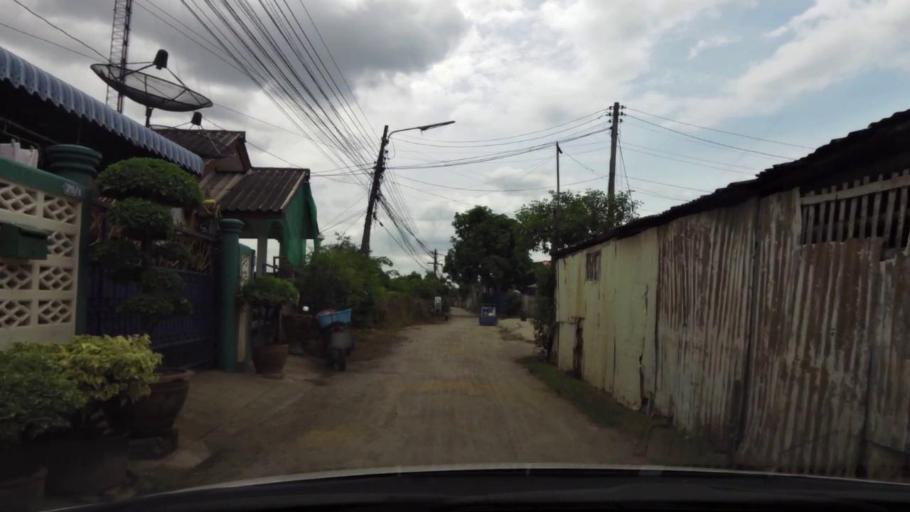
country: TH
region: Ratchaburi
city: Ratchaburi
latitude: 13.5326
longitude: 99.8255
